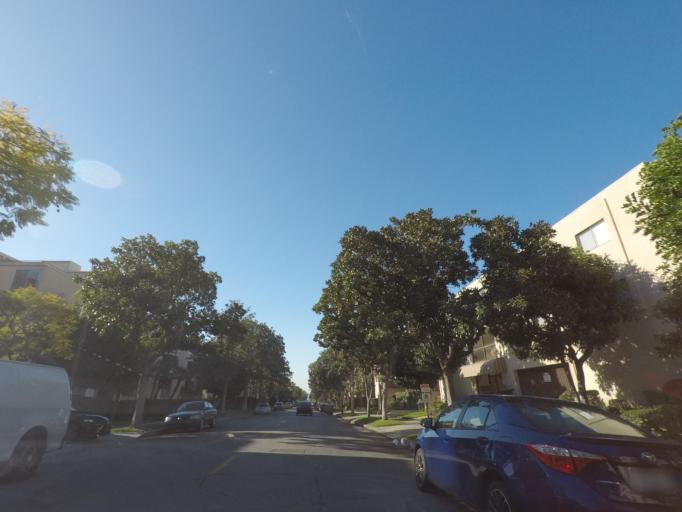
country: US
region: California
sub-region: Los Angeles County
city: Glendale
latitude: 34.1531
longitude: -118.2528
